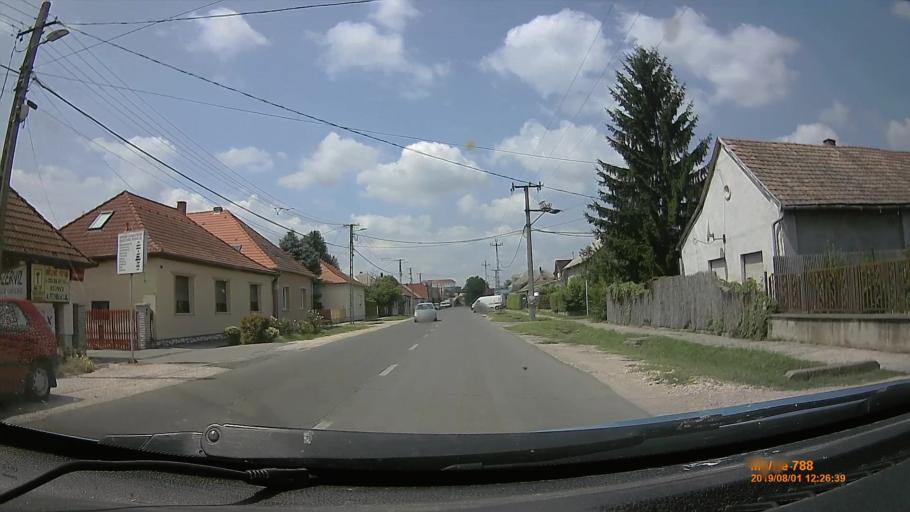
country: HU
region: Baranya
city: Siklos
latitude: 45.8521
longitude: 18.3101
